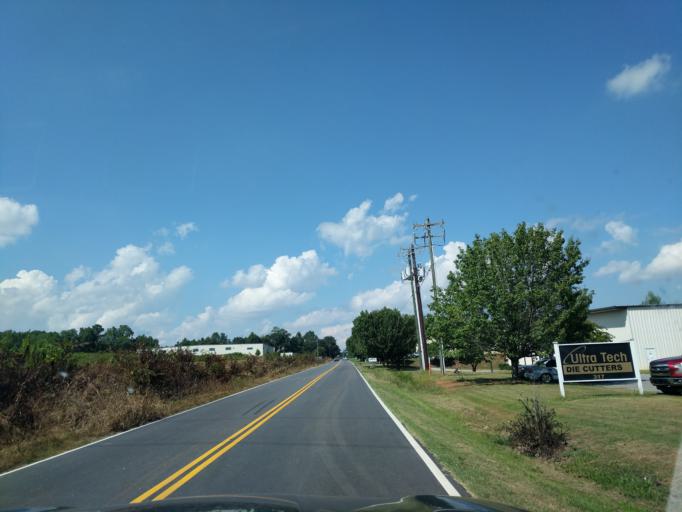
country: US
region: South Carolina
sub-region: Spartanburg County
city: Wellford
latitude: 34.8952
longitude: -82.1003
